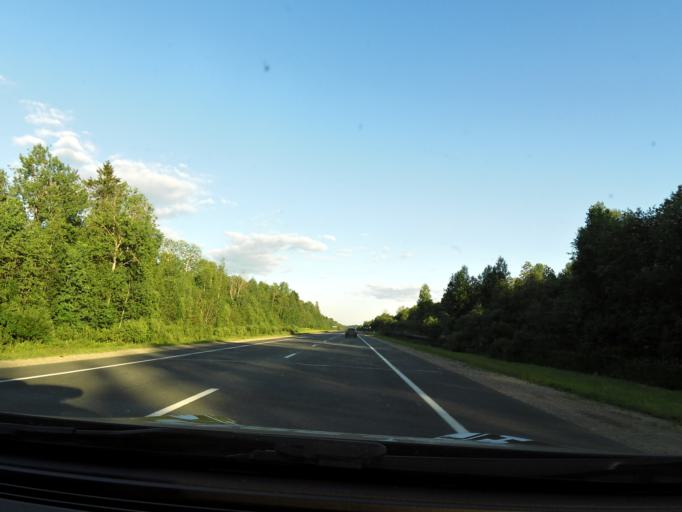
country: RU
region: Vologda
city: Vologda
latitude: 59.0997
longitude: 39.9929
